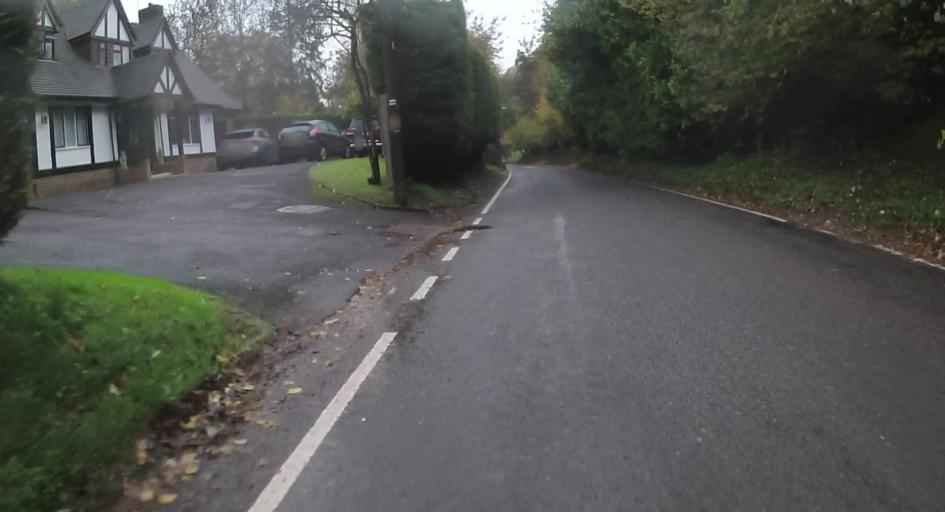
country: GB
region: England
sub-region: Hampshire
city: Alton
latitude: 51.1414
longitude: -1.0139
